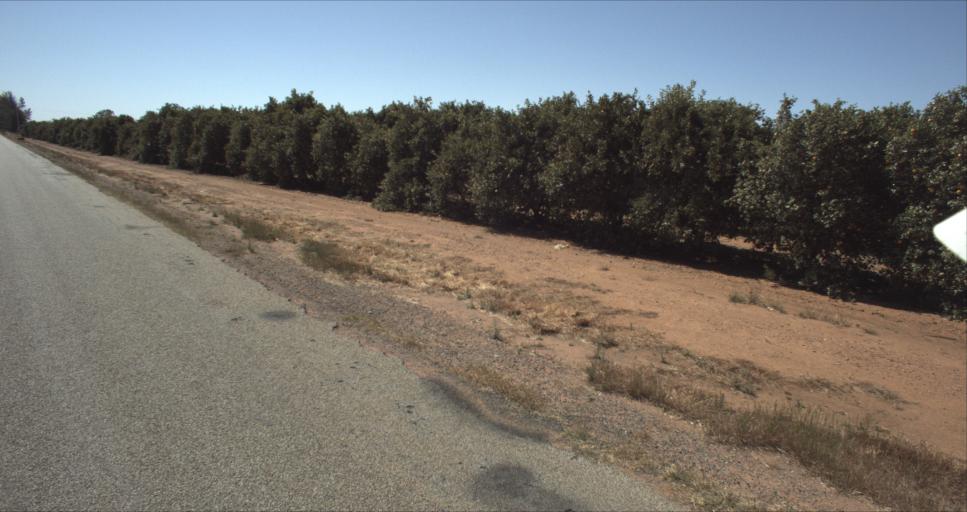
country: AU
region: New South Wales
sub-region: Leeton
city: Leeton
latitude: -34.5379
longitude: 146.3598
